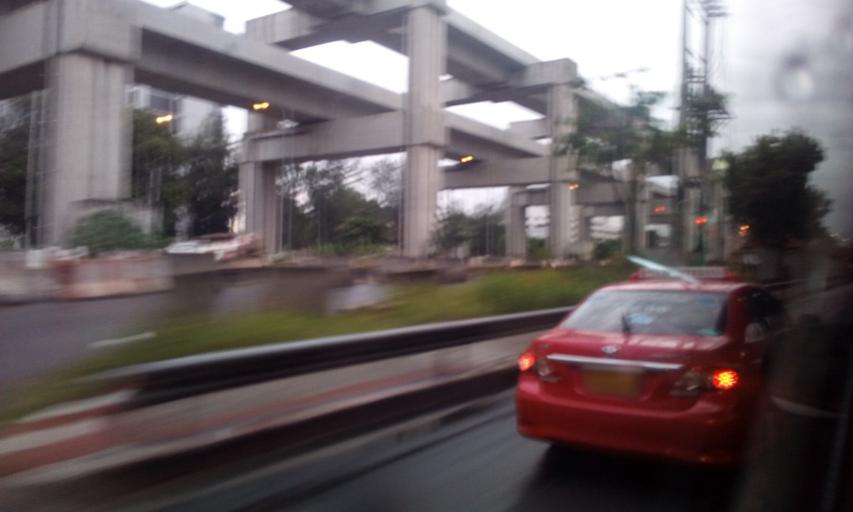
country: TH
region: Bangkok
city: Don Mueang
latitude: 13.9185
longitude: 100.6003
